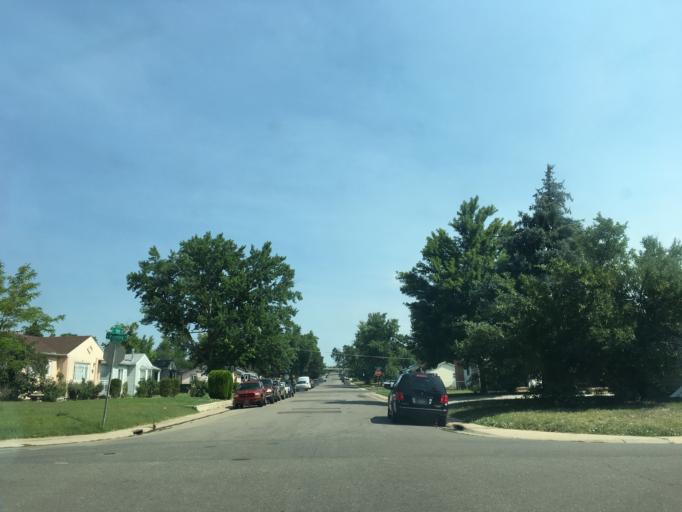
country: US
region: Colorado
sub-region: Jefferson County
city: Lakewood
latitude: 39.6923
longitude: -105.0507
